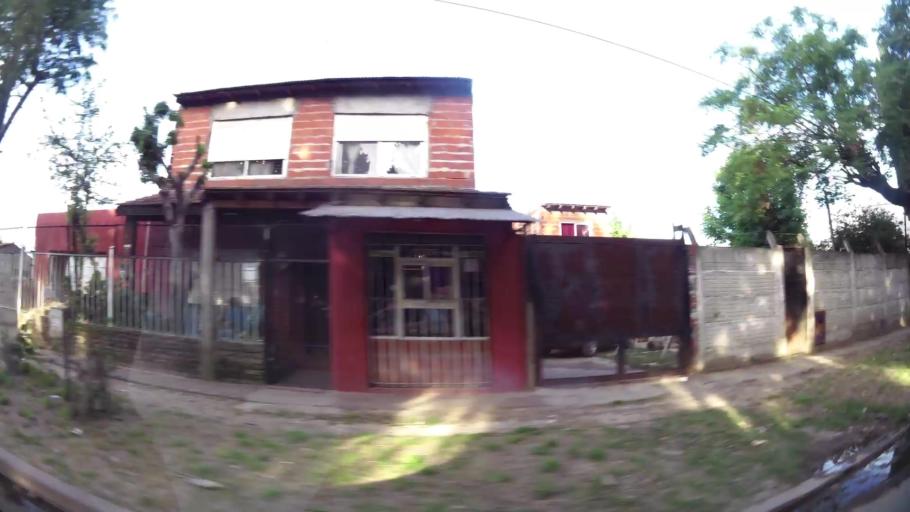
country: AR
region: Buenos Aires
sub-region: Partido de Almirante Brown
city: Adrogue
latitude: -34.7904
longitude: -58.3259
